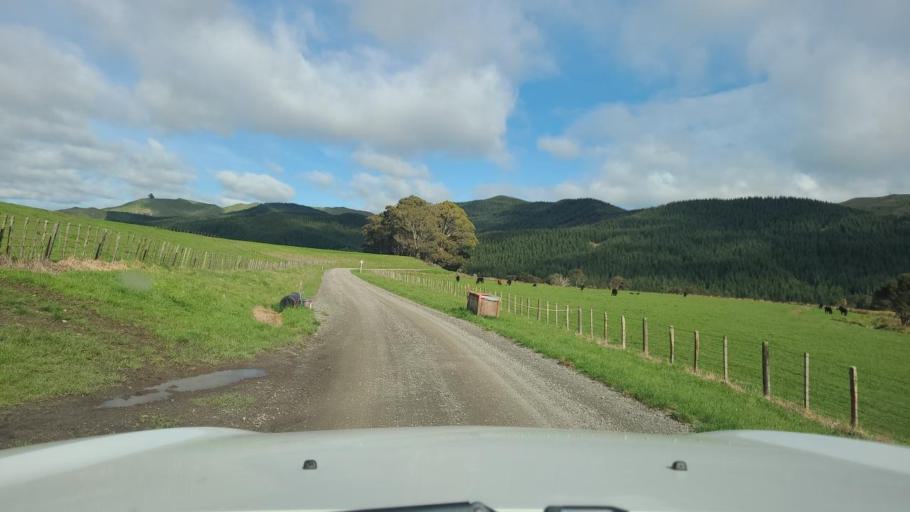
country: NZ
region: Wellington
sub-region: South Wairarapa District
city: Waipawa
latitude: -41.2647
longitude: 175.6779
